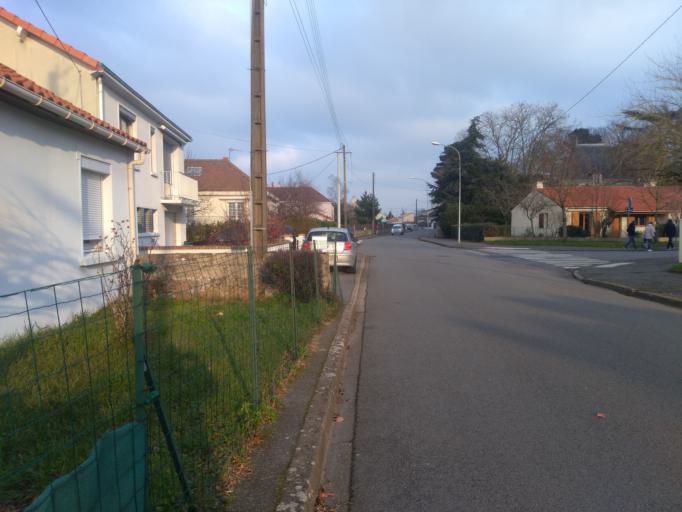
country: FR
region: Pays de la Loire
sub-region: Departement de la Loire-Atlantique
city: Saint-Sebastien-sur-Loire
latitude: 47.1945
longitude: -1.5066
